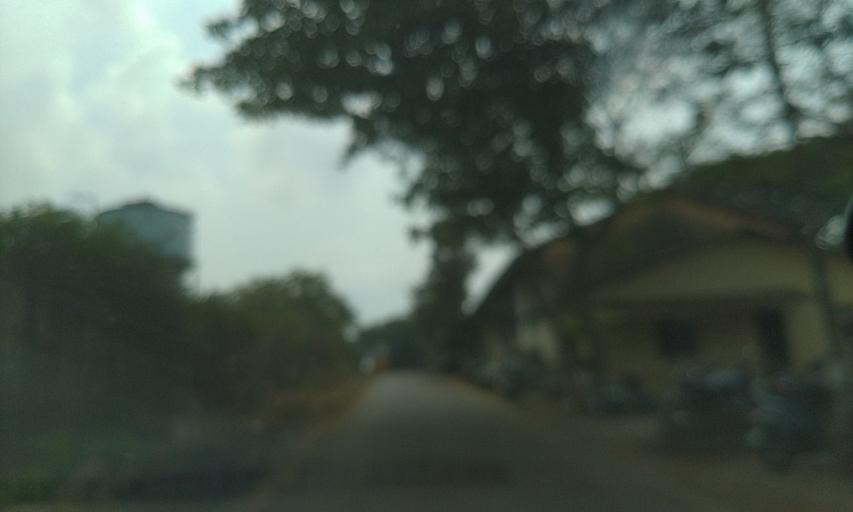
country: IN
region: Goa
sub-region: North Goa
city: Panaji
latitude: 15.4875
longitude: 73.8288
